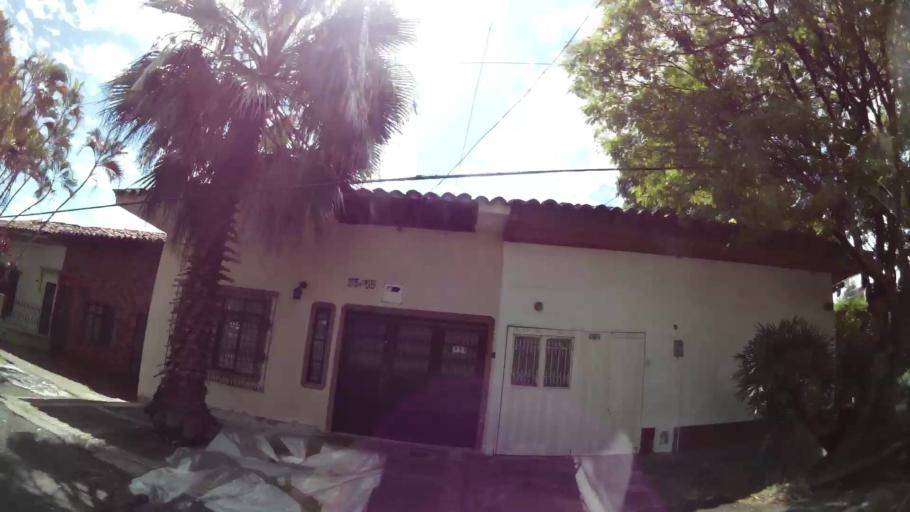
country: CO
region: Valle del Cauca
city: Cali
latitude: 3.4327
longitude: -76.5460
